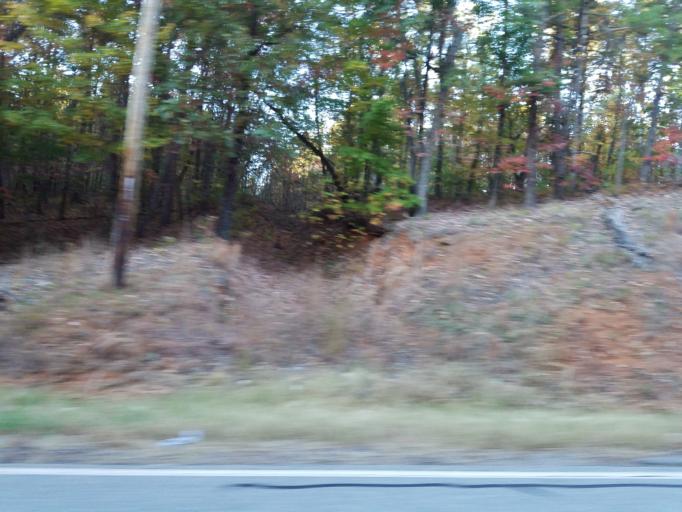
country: US
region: Georgia
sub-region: Dawson County
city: Dawsonville
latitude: 34.5482
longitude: -84.1434
